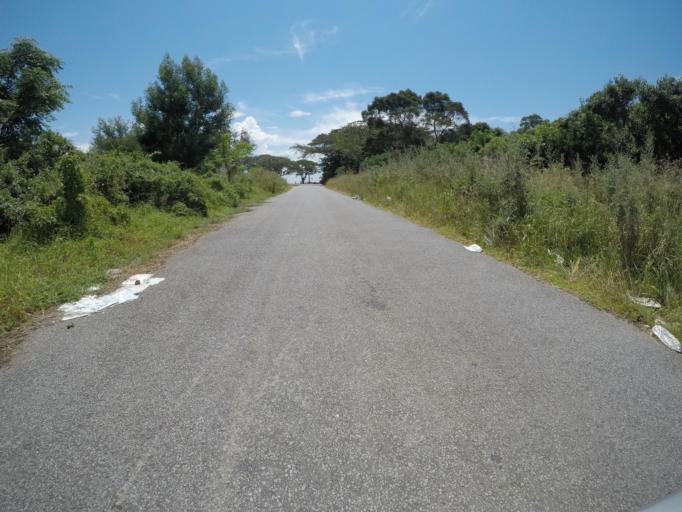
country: ZA
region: Eastern Cape
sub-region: Buffalo City Metropolitan Municipality
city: East London
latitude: -33.0364
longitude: 27.8456
